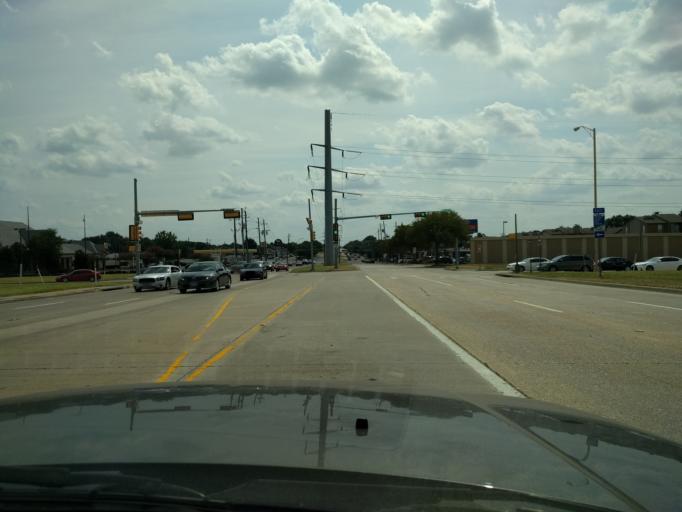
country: US
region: Texas
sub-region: Dallas County
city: Addison
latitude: 33.0126
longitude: -96.8437
